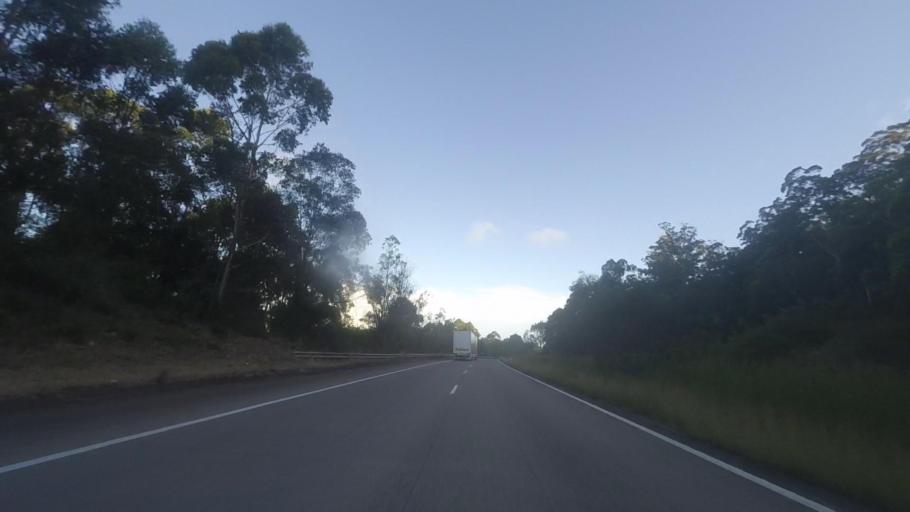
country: AU
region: New South Wales
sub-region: Great Lakes
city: Bulahdelah
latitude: -32.2853
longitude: 152.3396
